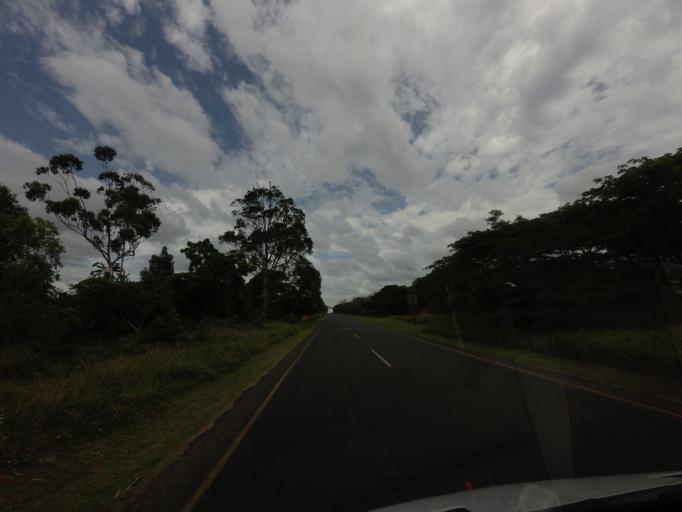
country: ZA
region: KwaZulu-Natal
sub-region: uMkhanyakude District Municipality
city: Mtubatuba
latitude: -28.3741
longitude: 32.3924
